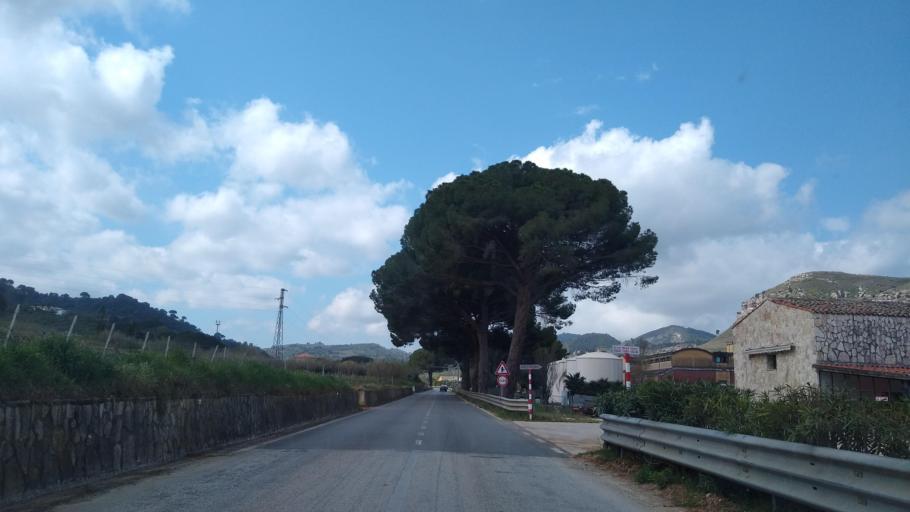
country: IT
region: Sicily
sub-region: Trapani
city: Calatafimi
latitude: 37.9424
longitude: 12.8583
